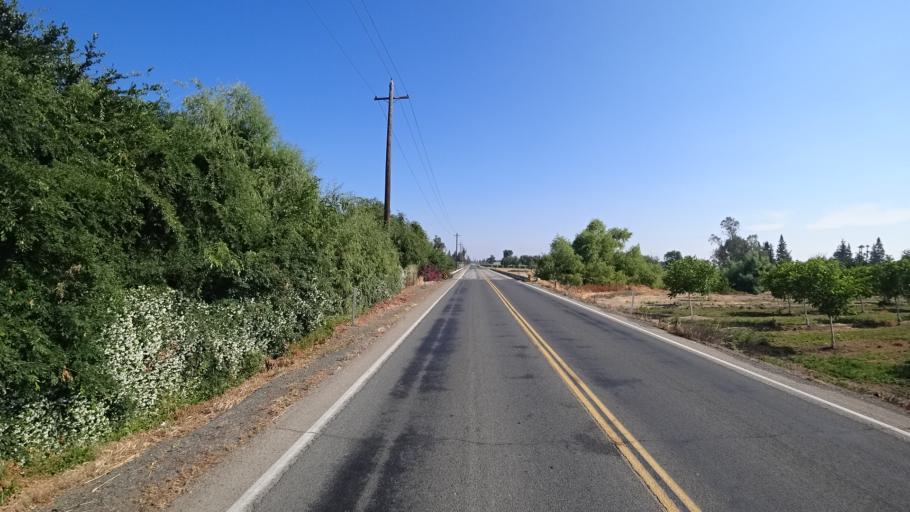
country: US
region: California
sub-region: Fresno County
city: Kingsburg
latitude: 36.4839
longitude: -119.5573
